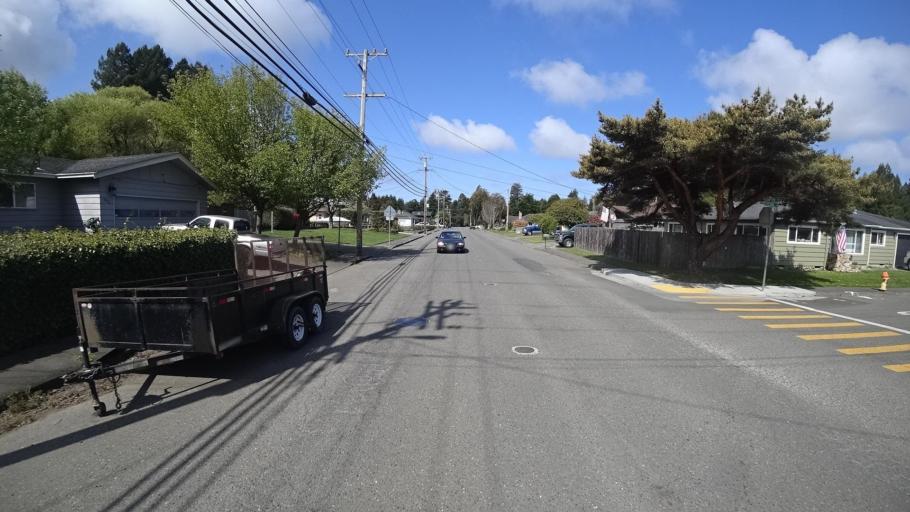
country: US
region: California
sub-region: Humboldt County
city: Cutten
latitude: 40.7587
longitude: -124.1496
